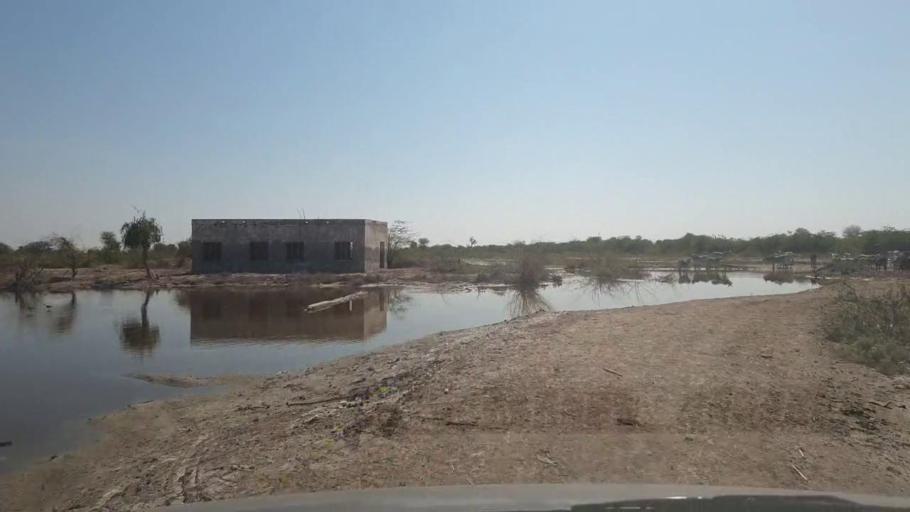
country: PK
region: Sindh
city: Dhoro Naro
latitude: 25.4430
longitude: 69.6097
